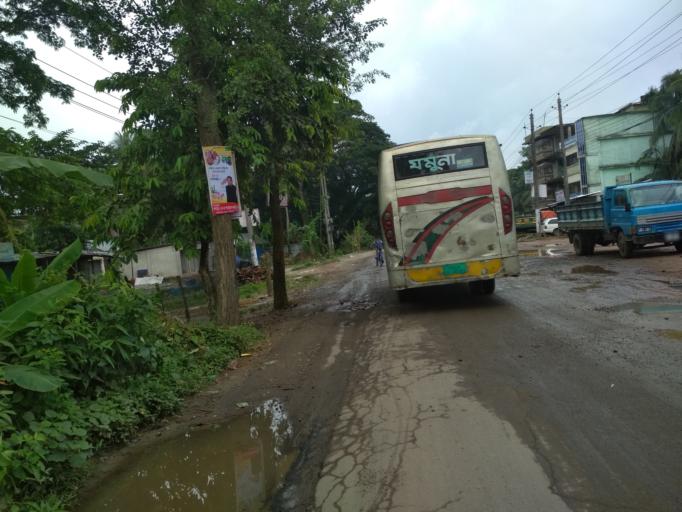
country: BD
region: Chittagong
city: Lakshmipur
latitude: 22.9458
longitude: 90.8179
